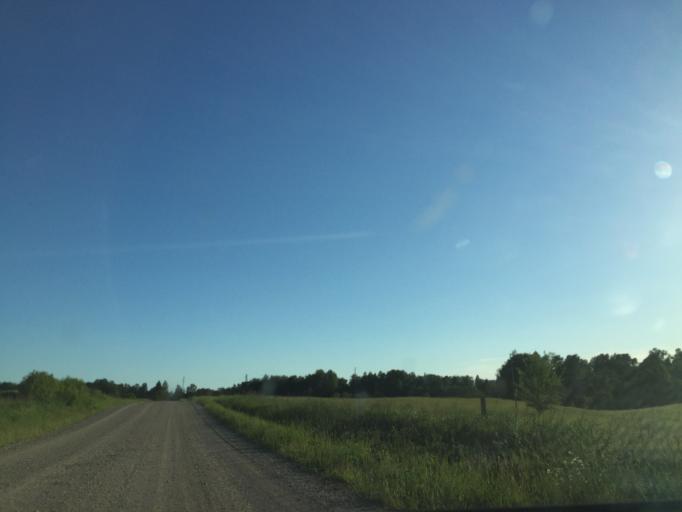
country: LV
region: Broceni
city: Broceni
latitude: 56.8290
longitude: 22.5591
